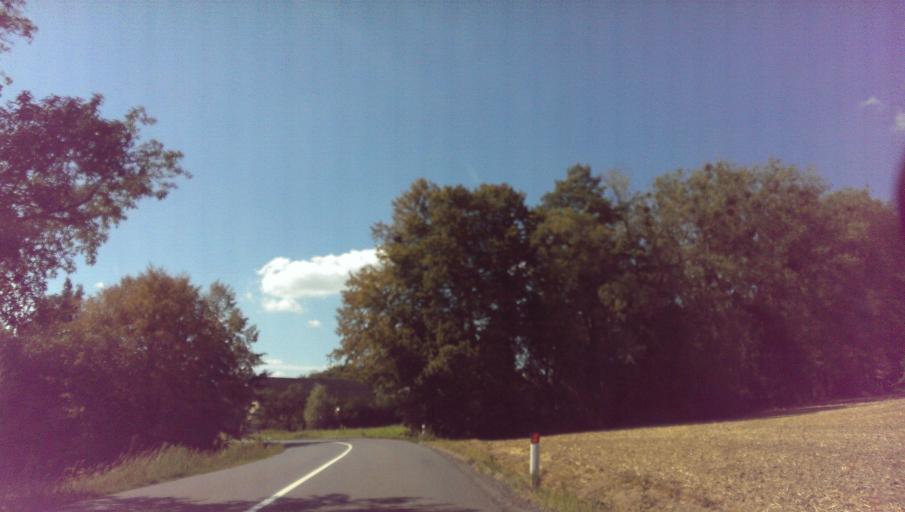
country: CZ
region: Zlin
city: Valasske Mezirici
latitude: 49.4629
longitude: 17.9255
